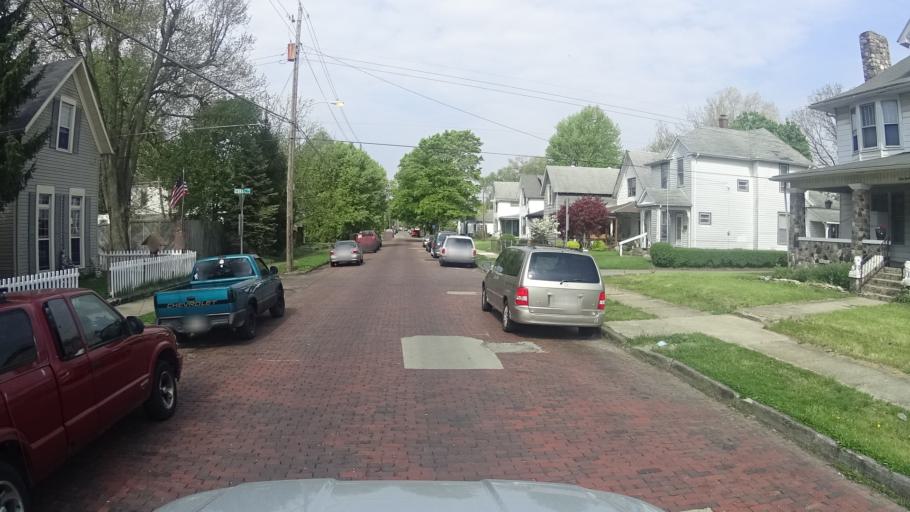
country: US
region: Indiana
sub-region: Madison County
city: Anderson
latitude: 40.1089
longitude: -85.6833
